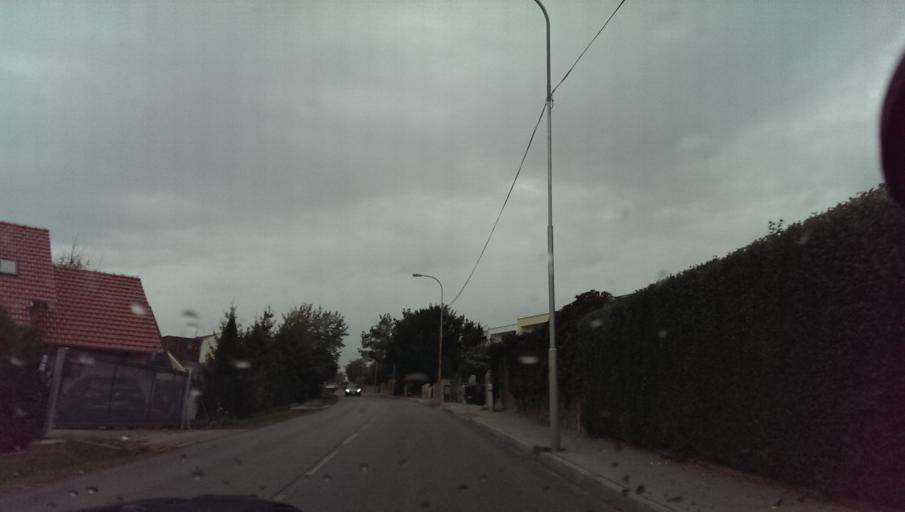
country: CZ
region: South Moravian
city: Moravany
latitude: 49.1476
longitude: 16.5731
